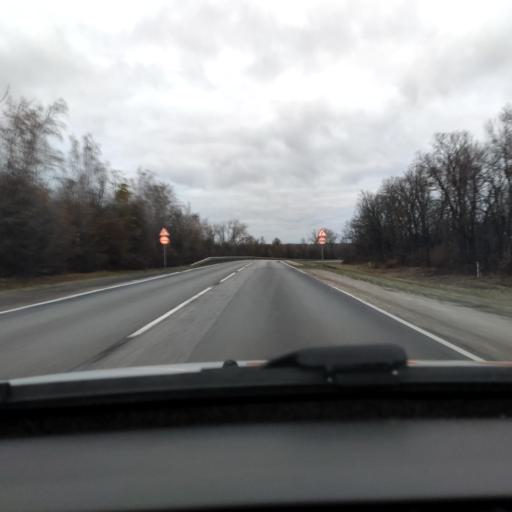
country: RU
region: Lipetsk
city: Khlevnoye
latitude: 52.3163
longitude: 39.1663
